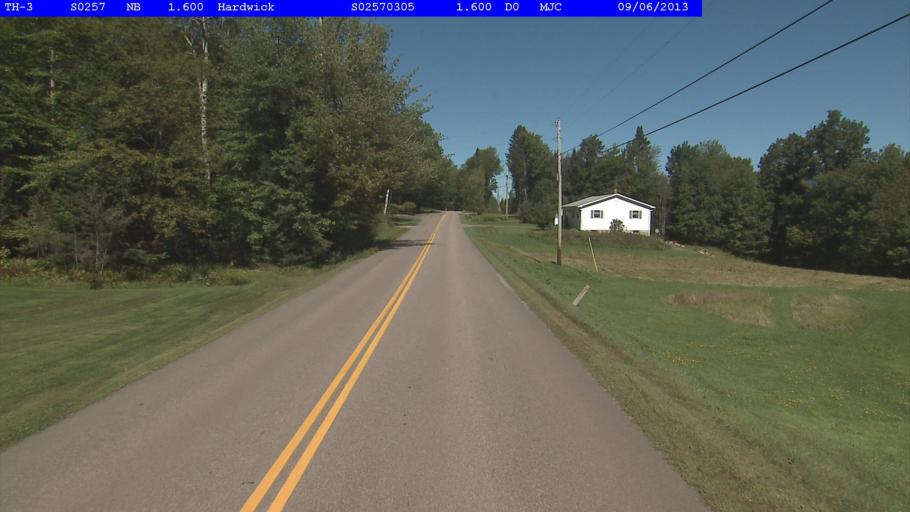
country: US
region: Vermont
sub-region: Caledonia County
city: Hardwick
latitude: 44.5142
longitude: -72.3422
